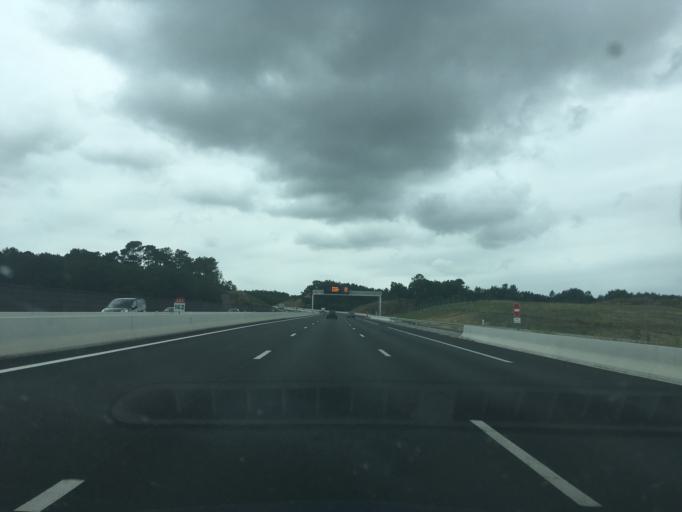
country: FR
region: Aquitaine
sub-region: Departement des Landes
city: Labenne
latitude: 43.5775
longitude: -1.4253
